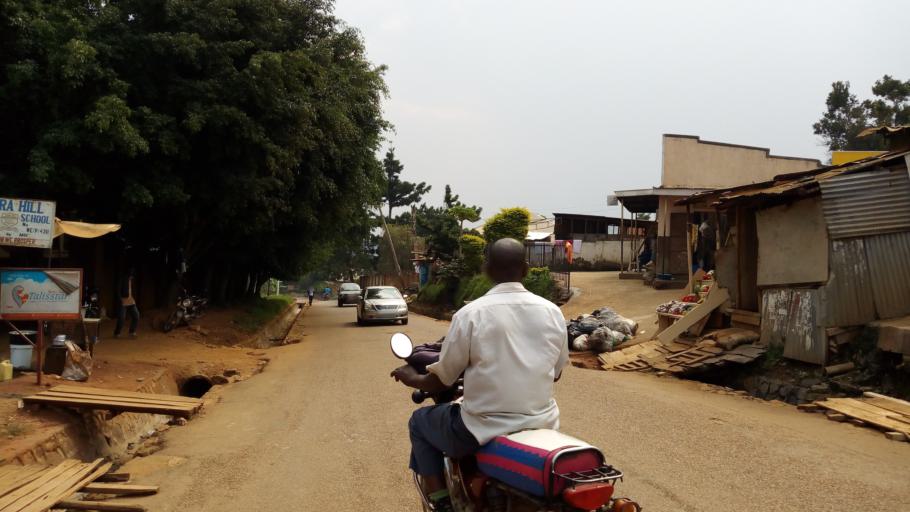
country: UG
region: Central Region
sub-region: Wakiso District
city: Kireka
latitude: 0.3095
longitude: 32.6423
